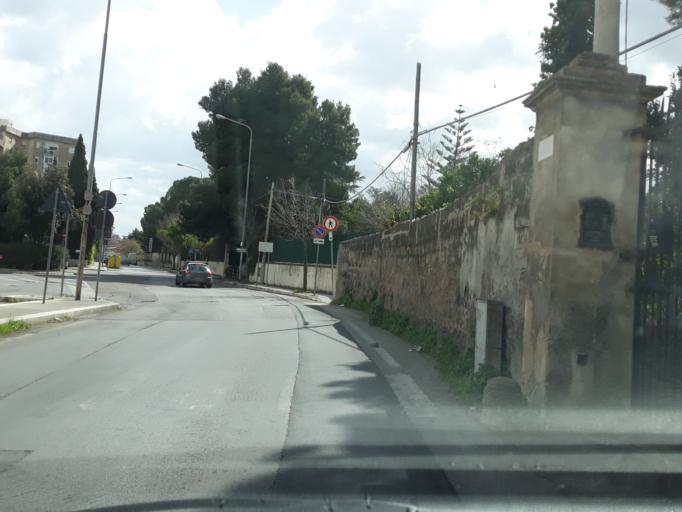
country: IT
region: Sicily
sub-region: Palermo
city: Palermo
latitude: 38.1241
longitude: 13.3177
